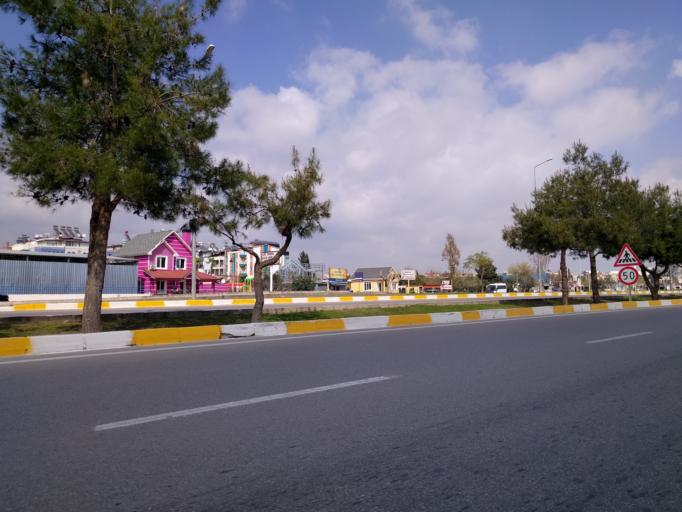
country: TR
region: Antalya
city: Antalya
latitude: 36.9011
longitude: 30.6457
